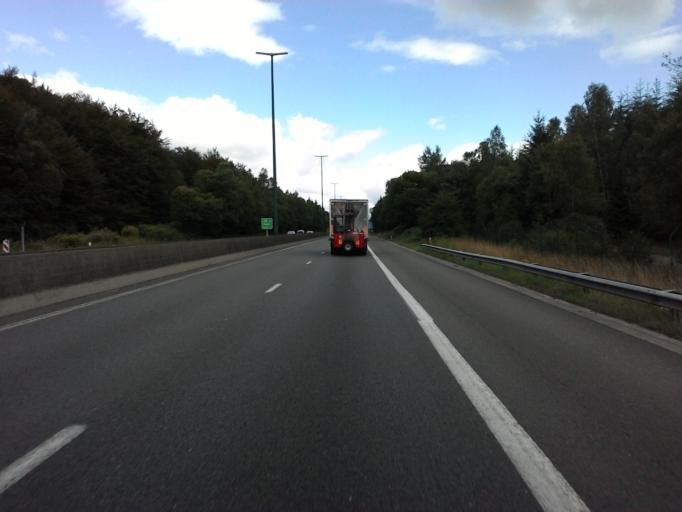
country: BE
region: Wallonia
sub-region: Province du Luxembourg
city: Habay-la-Vieille
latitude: 49.7336
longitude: 5.5783
